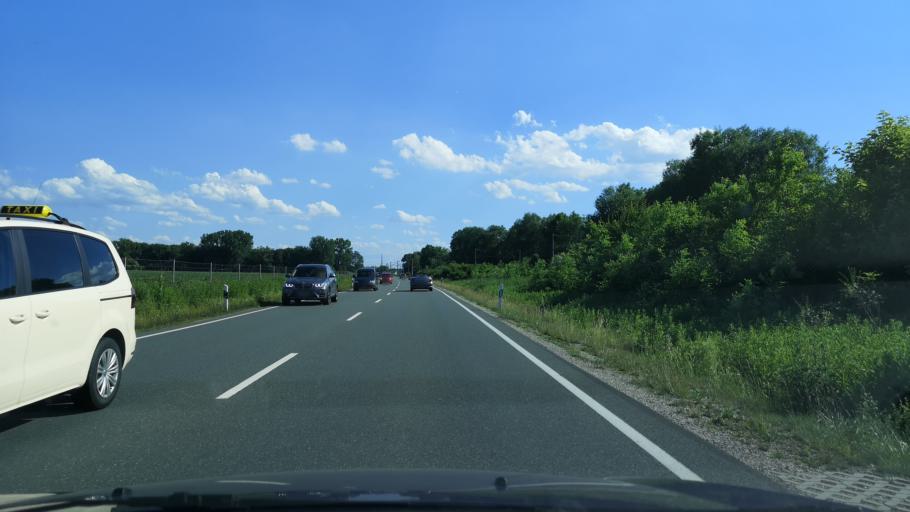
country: DE
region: Bavaria
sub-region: Upper Bavaria
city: Hallbergmoos
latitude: 48.2986
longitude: 11.7112
